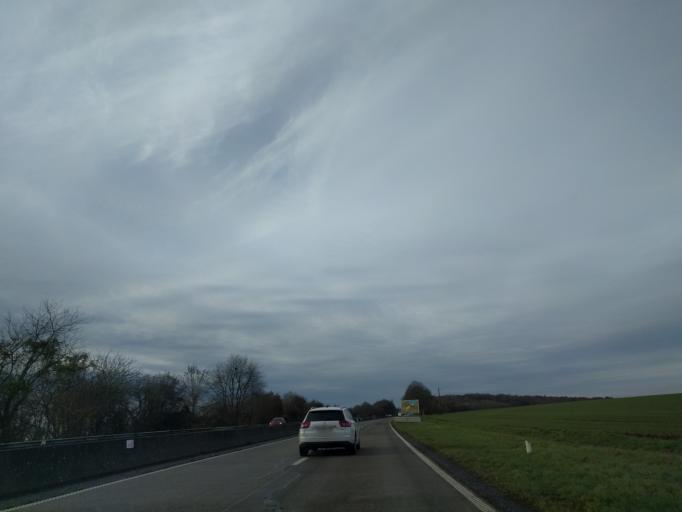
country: BE
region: Wallonia
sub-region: Province de Namur
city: Houyet
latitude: 50.2428
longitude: 4.9942
